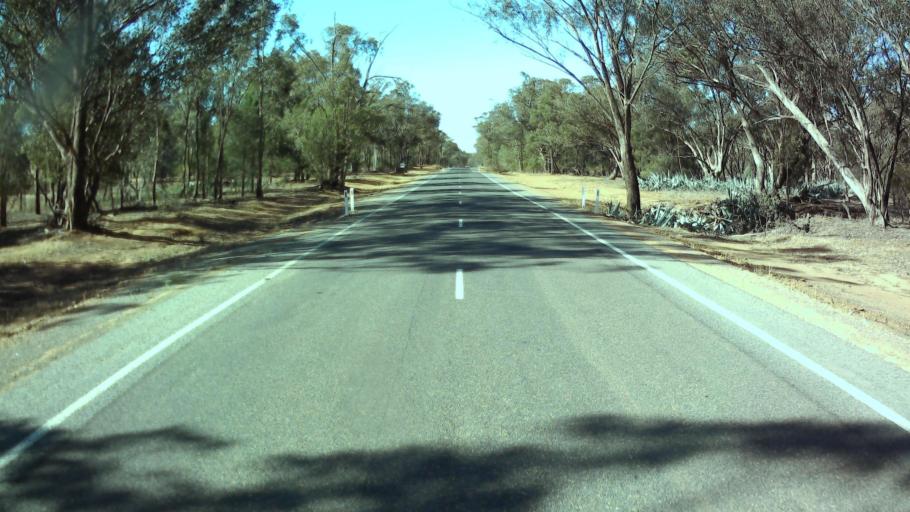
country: AU
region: New South Wales
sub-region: Weddin
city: Grenfell
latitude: -33.7525
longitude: 148.0840
